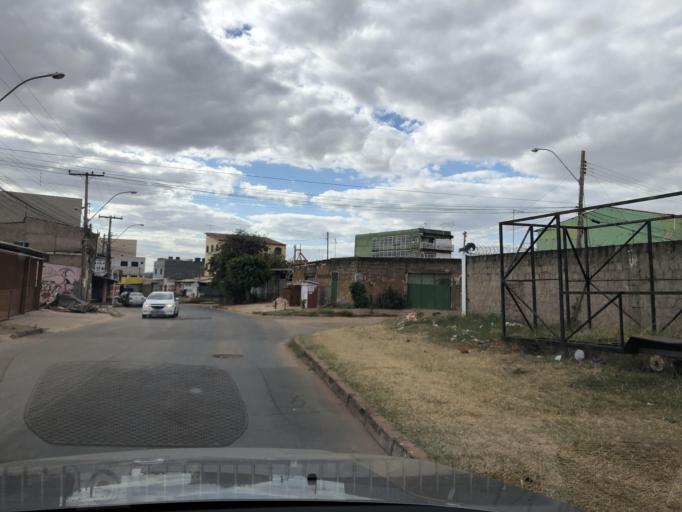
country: BR
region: Federal District
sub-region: Brasilia
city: Brasilia
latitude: -15.8813
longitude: -48.1118
